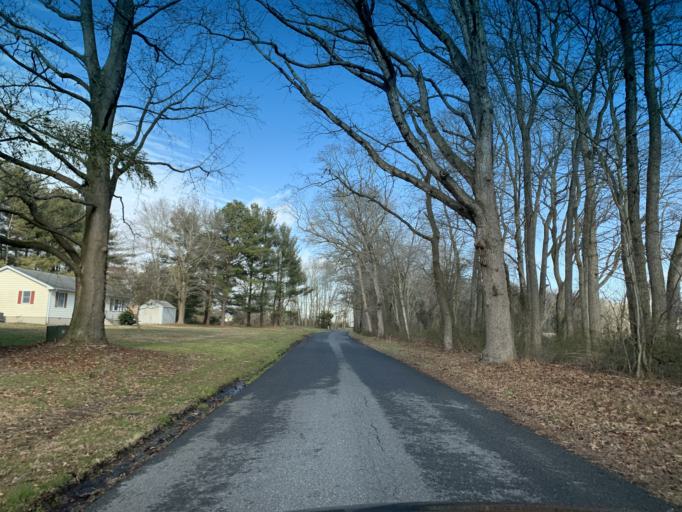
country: US
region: Delaware
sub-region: Sussex County
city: Selbyville
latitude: 38.4419
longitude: -75.1902
